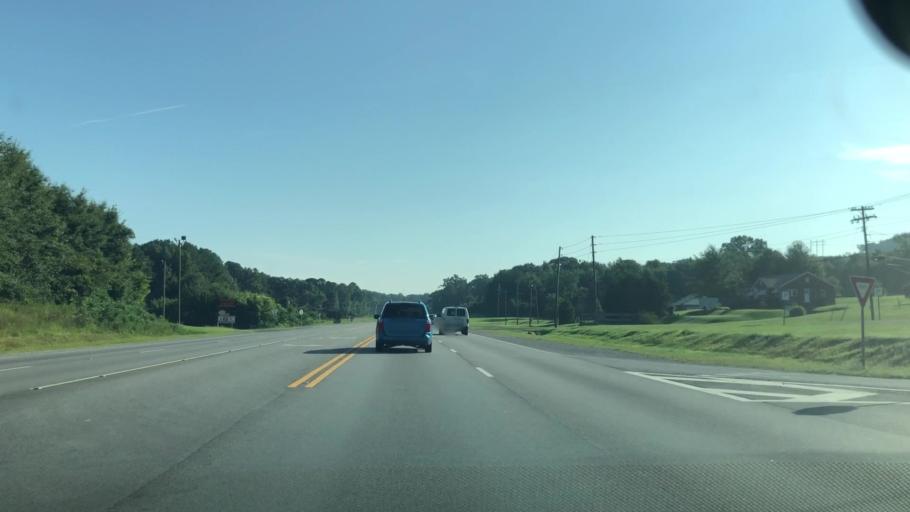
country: US
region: Alabama
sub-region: Calhoun County
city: Bynum
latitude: 33.6250
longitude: -85.9197
